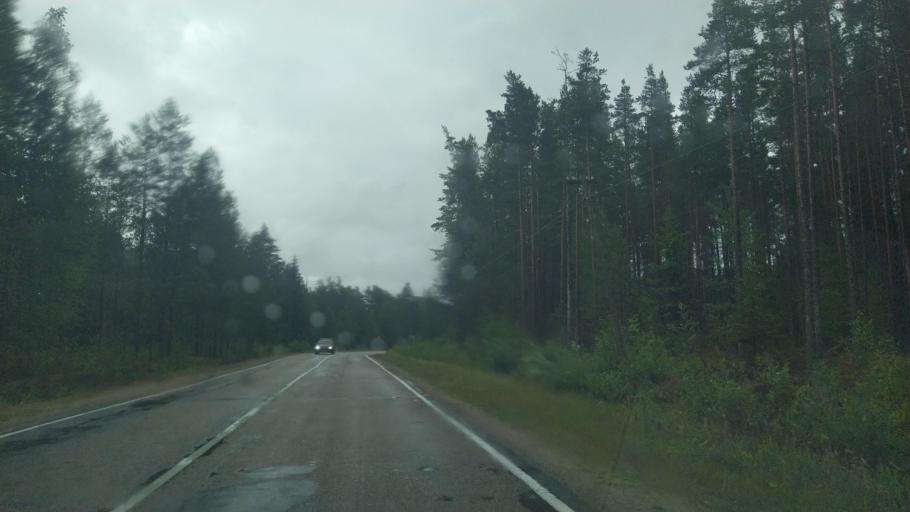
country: RU
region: Leningrad
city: Priozersk
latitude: 60.9776
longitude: 30.2762
